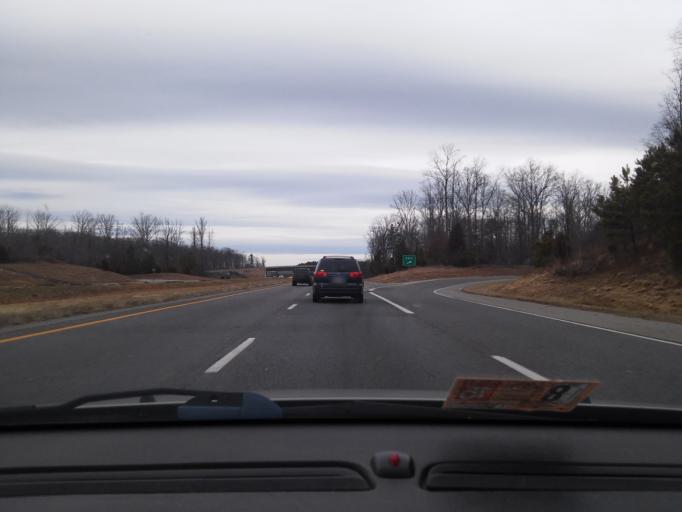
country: US
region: Virginia
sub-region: Henrico County
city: Short Pump
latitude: 37.6330
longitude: -77.6636
